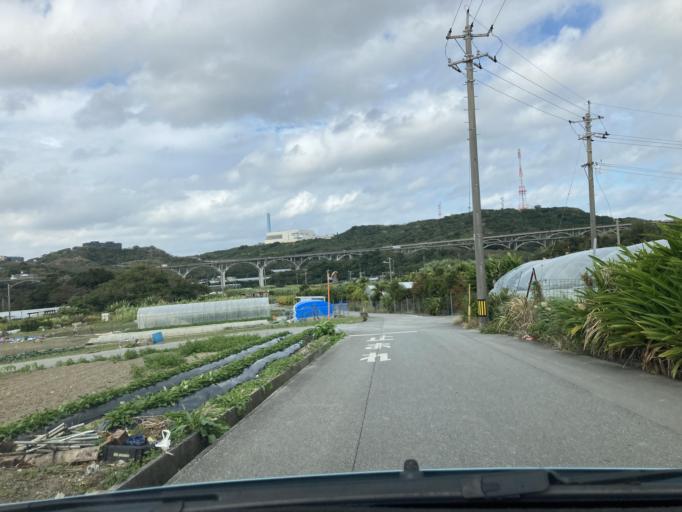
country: JP
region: Okinawa
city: Ginowan
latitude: 26.2098
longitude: 127.7432
